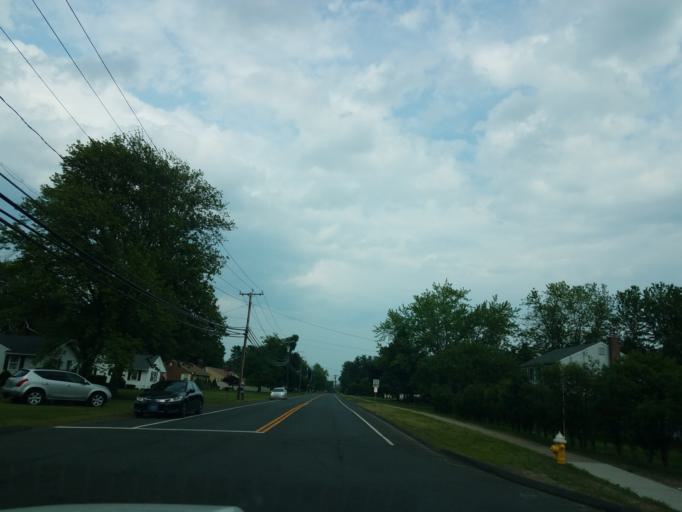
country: US
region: Connecticut
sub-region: Hartford County
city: Windsor Locks
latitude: 41.9265
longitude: -72.6554
